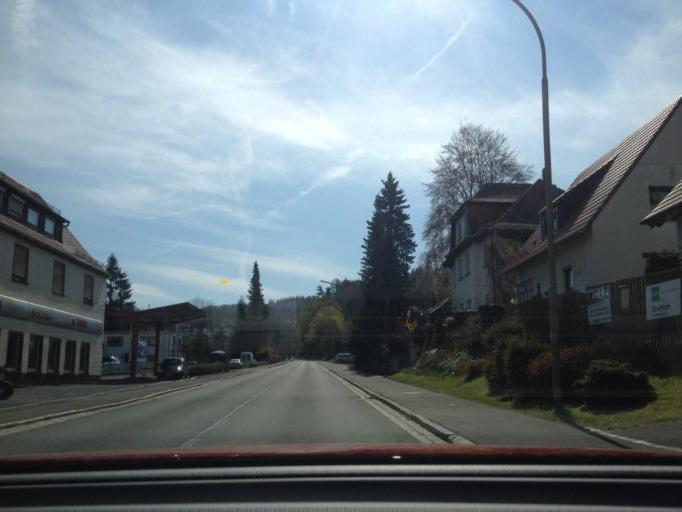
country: DE
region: Bavaria
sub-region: Upper Franconia
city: Gefrees
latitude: 50.0941
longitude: 11.7451
